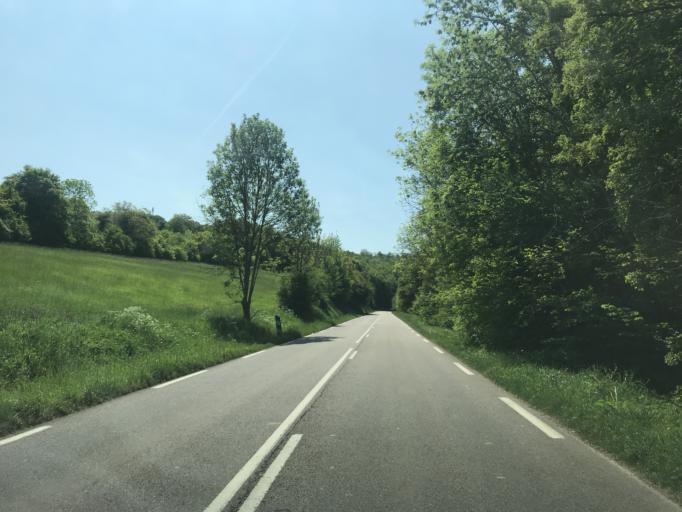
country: FR
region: Haute-Normandie
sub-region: Departement de l'Eure
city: Saint-Aubin-sur-Gaillon
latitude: 49.0850
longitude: 1.2633
